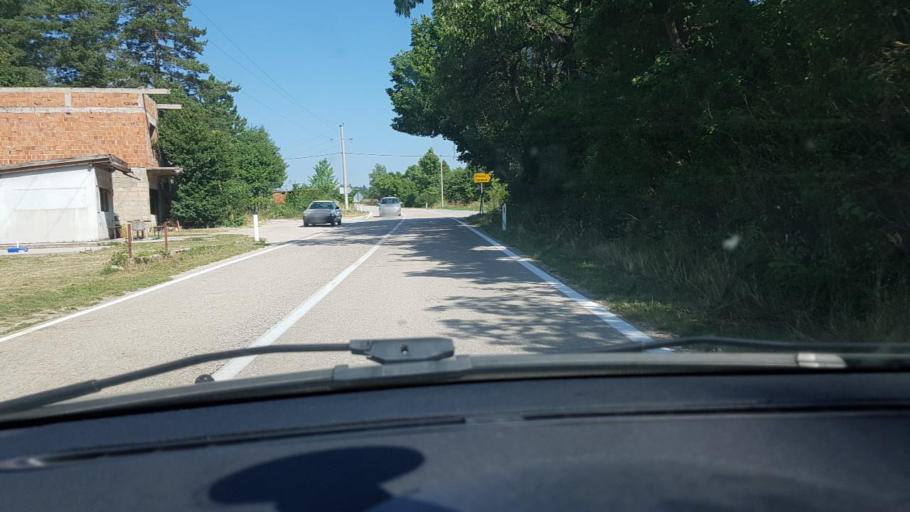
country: BA
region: Federation of Bosnia and Herzegovina
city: Bosansko Grahovo
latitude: 44.0912
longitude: 16.5639
